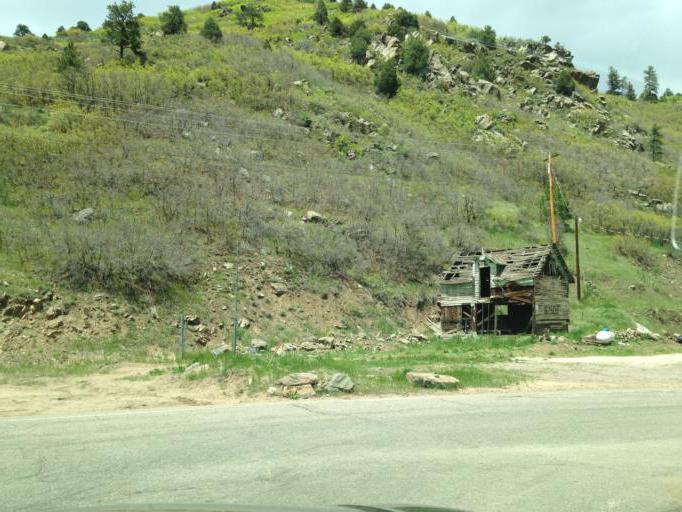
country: US
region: Colorado
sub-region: Jefferson County
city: Ken Caryl
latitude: 39.5369
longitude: -105.1868
